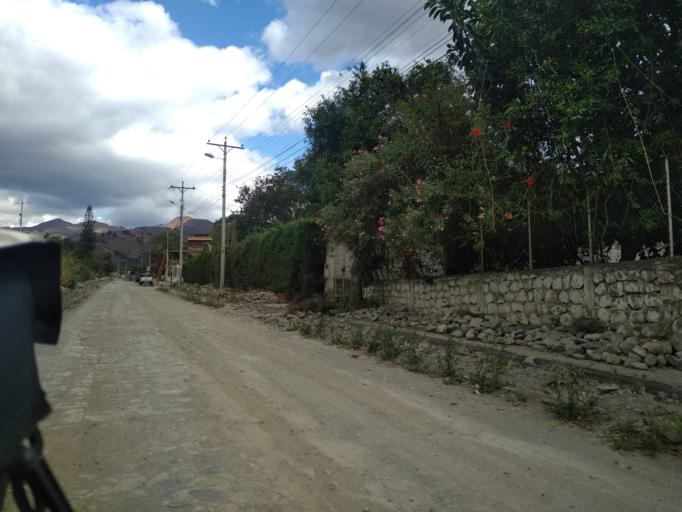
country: EC
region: Loja
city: Loja
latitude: -4.2547
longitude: -79.2232
